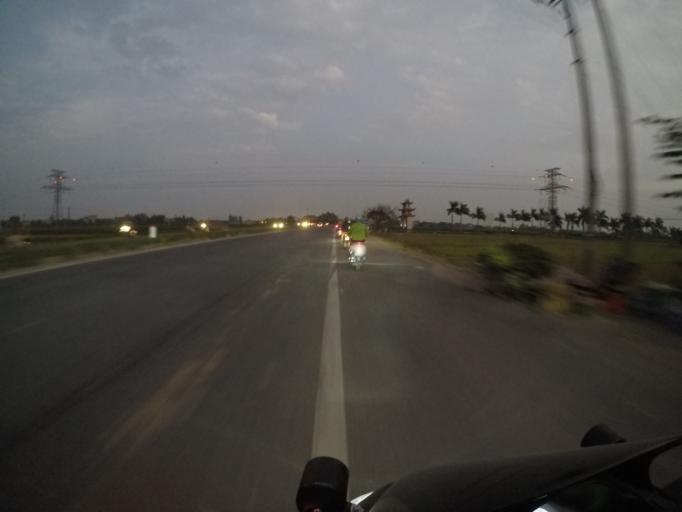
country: VN
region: Vinh Phuc
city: Phuc Yen
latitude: 21.2347
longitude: 105.7481
